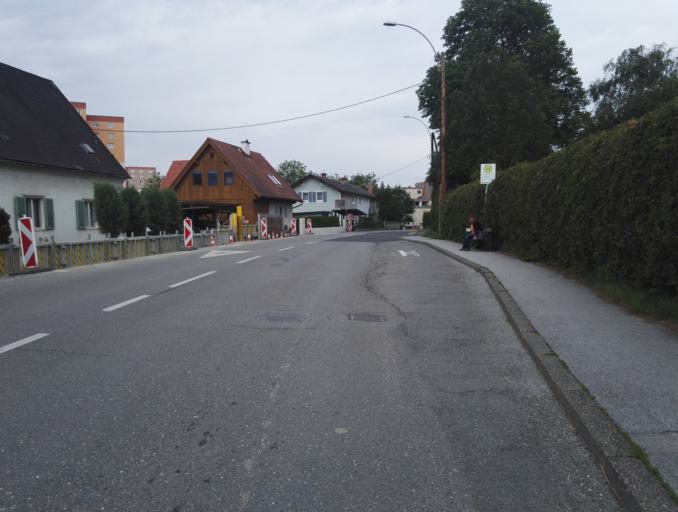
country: AT
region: Styria
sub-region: Graz Stadt
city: Mariatrost
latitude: 47.0760
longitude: 15.5003
